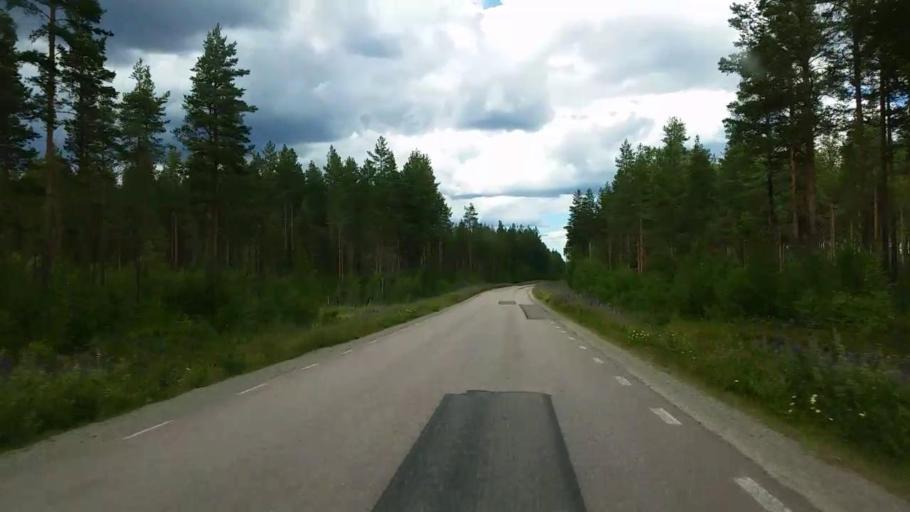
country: SE
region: Gaevleborg
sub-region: Ovanakers Kommun
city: Edsbyn
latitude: 61.4079
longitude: 15.8968
